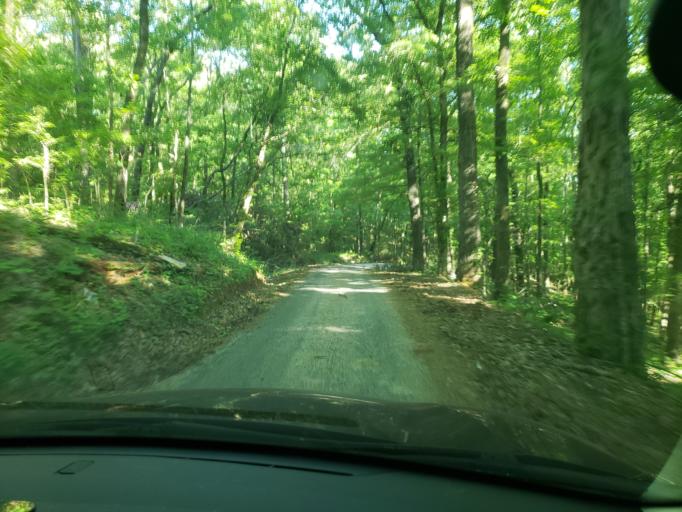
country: US
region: Alabama
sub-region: Elmore County
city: Tallassee
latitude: 32.5950
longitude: -85.8767
